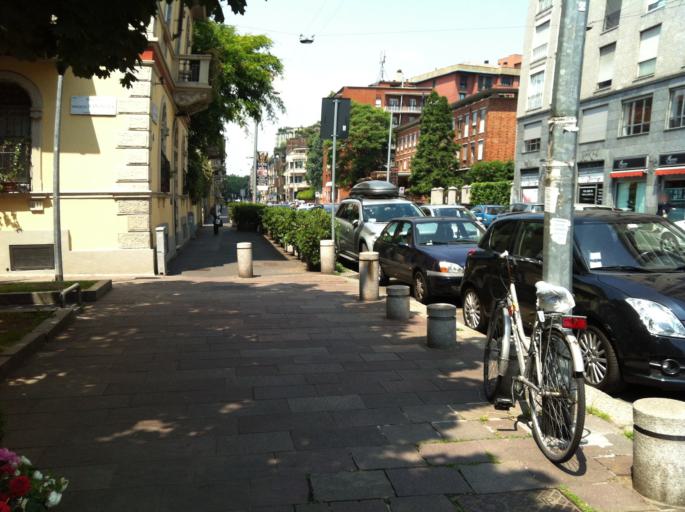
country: IT
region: Lombardy
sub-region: Citta metropolitana di Milano
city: Milano
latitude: 45.4707
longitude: 9.2112
